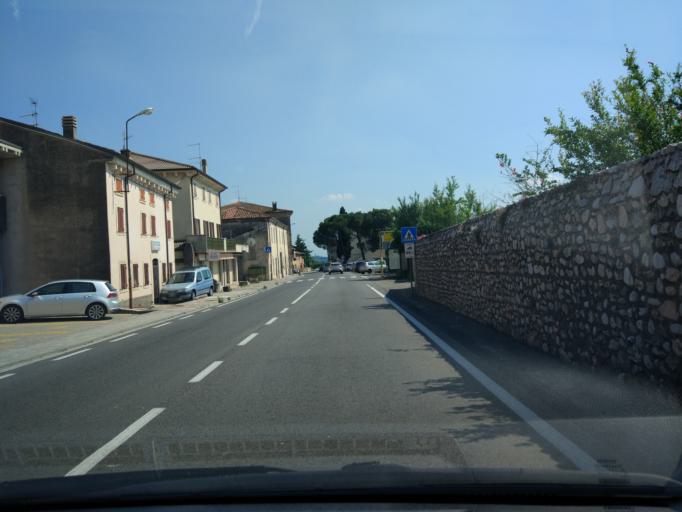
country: IT
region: Veneto
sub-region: Provincia di Verona
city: Cellore
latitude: 45.4850
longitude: 11.1771
